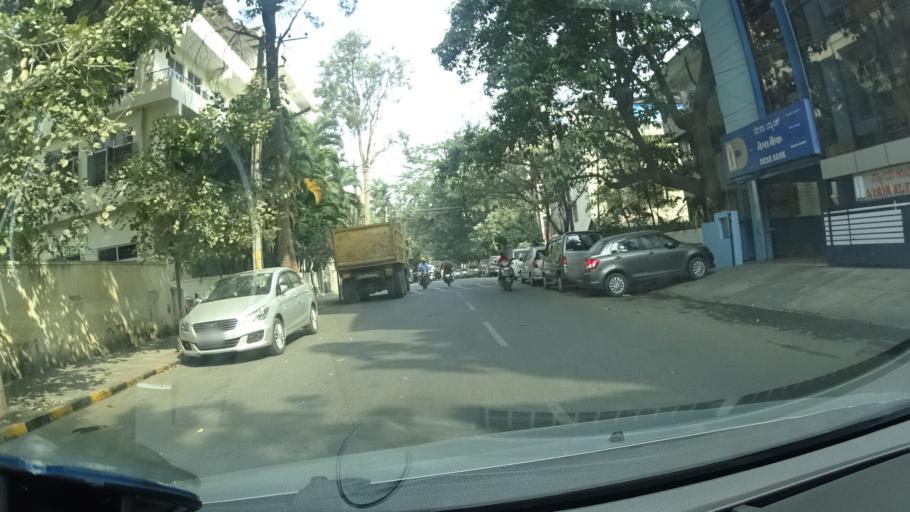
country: IN
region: Karnataka
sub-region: Bangalore Urban
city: Bangalore
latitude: 13.0008
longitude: 77.5683
